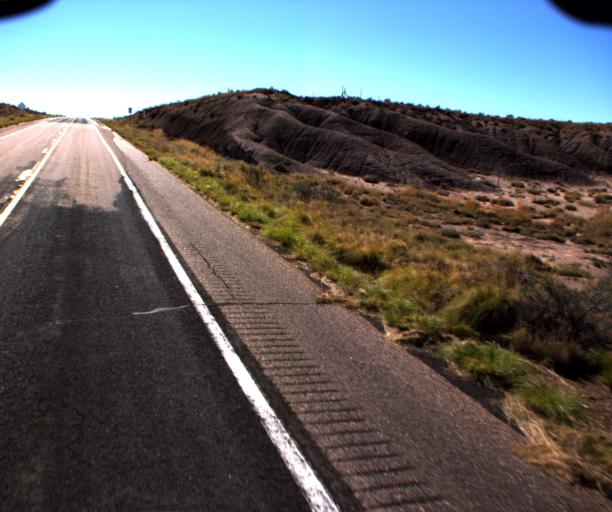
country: US
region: Arizona
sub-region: Navajo County
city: Snowflake
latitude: 34.7175
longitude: -109.7695
